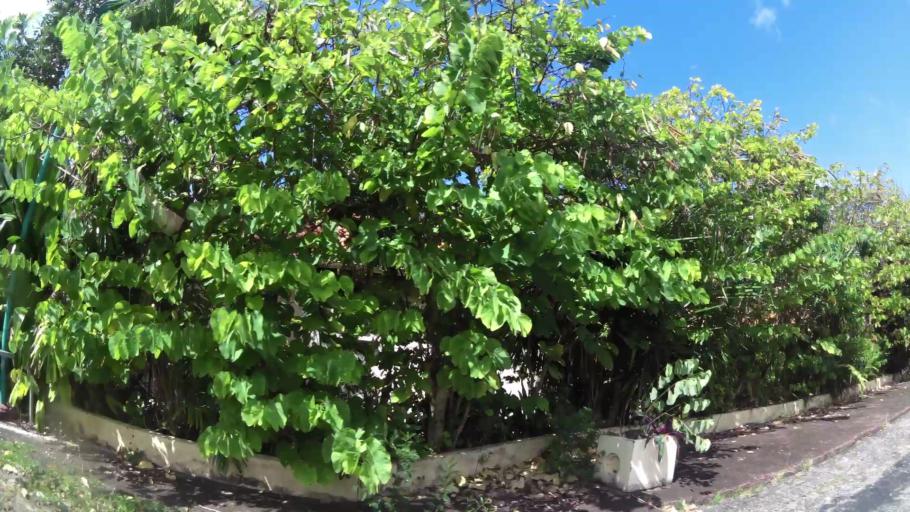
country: MQ
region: Martinique
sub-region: Martinique
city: Le Marin
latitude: 14.4424
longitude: -60.8763
